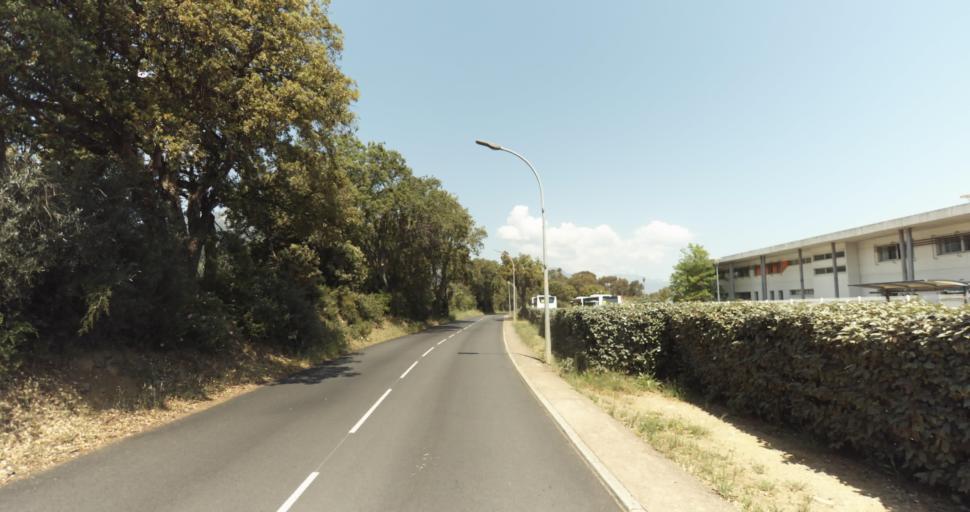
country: FR
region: Corsica
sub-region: Departement de la Haute-Corse
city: Biguglia
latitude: 42.5976
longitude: 9.4360
